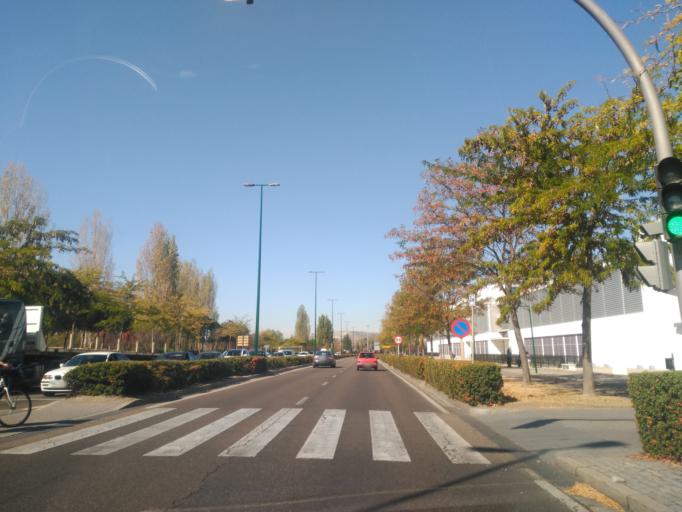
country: ES
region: Castille and Leon
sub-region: Provincia de Valladolid
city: Valladolid
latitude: 41.6226
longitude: -4.7489
